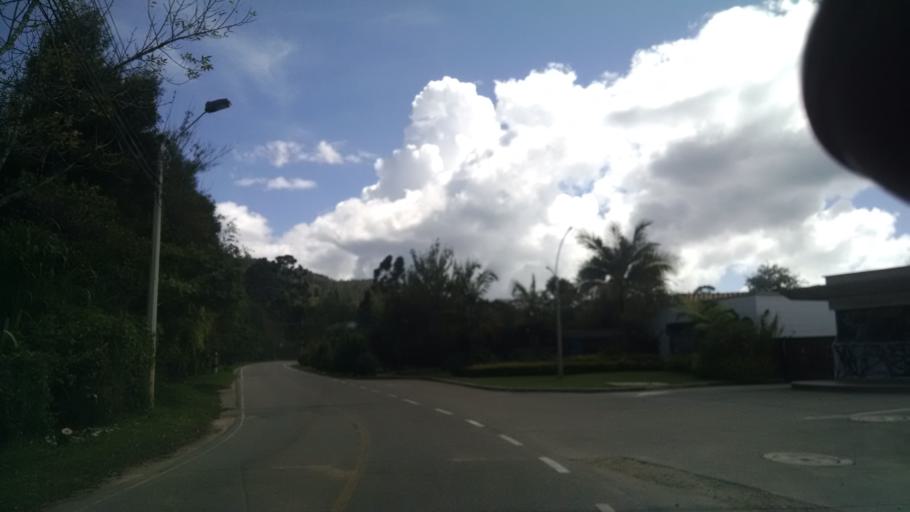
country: CO
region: Antioquia
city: El Retiro
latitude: 6.0760
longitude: -75.4984
